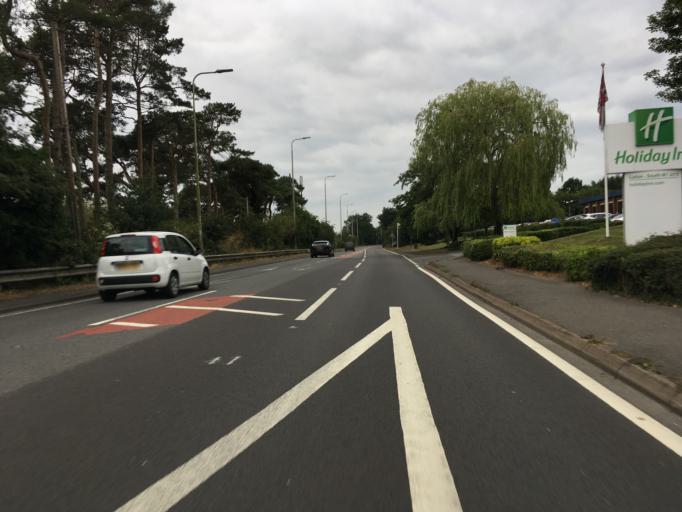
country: GB
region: England
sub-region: Hertfordshire
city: Flamstead
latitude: 51.8285
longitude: -0.4446
